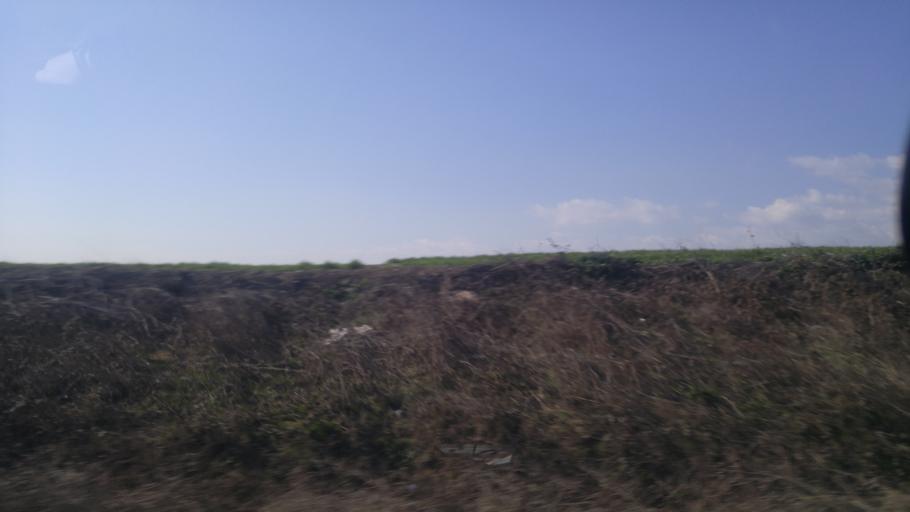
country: TR
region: Istanbul
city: Canta
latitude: 41.1004
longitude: 28.1106
